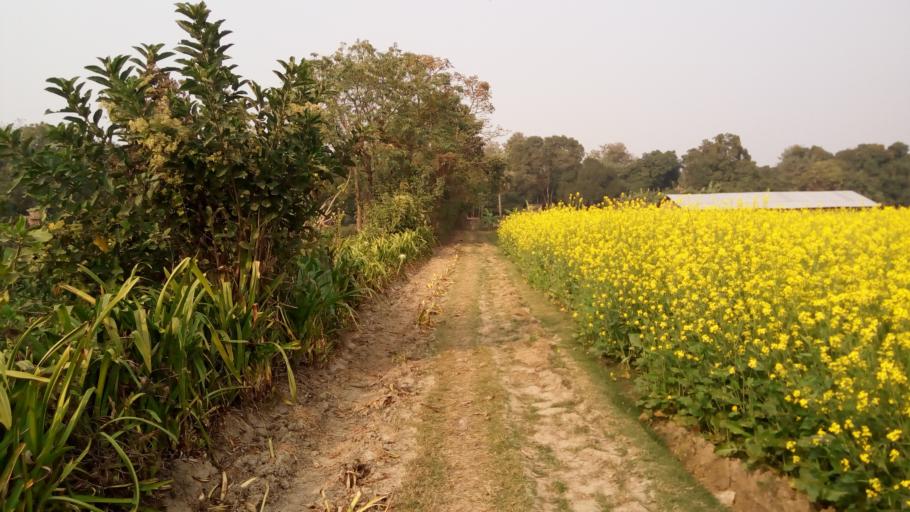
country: IN
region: West Bengal
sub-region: Nadia
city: Navadwip
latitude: 23.4459
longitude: 88.4177
